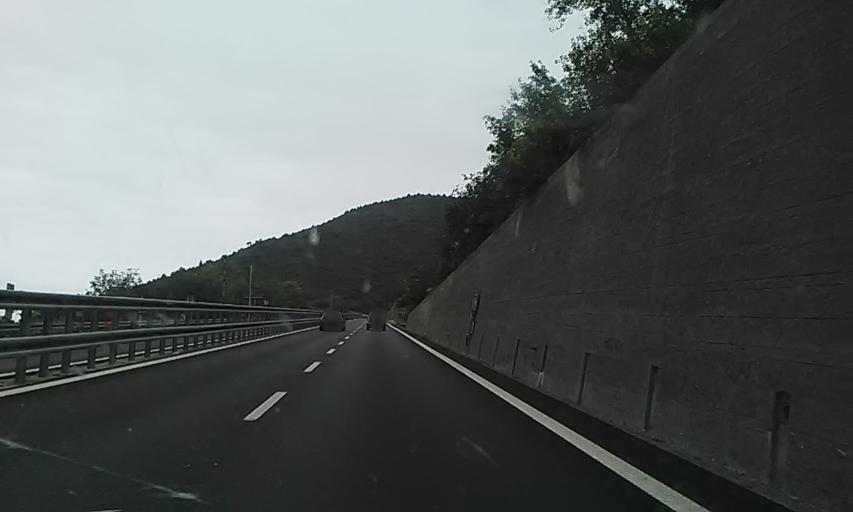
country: IT
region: Liguria
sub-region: Provincia di Savona
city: Borghetto Santo Spirito
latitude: 44.1147
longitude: 8.2284
